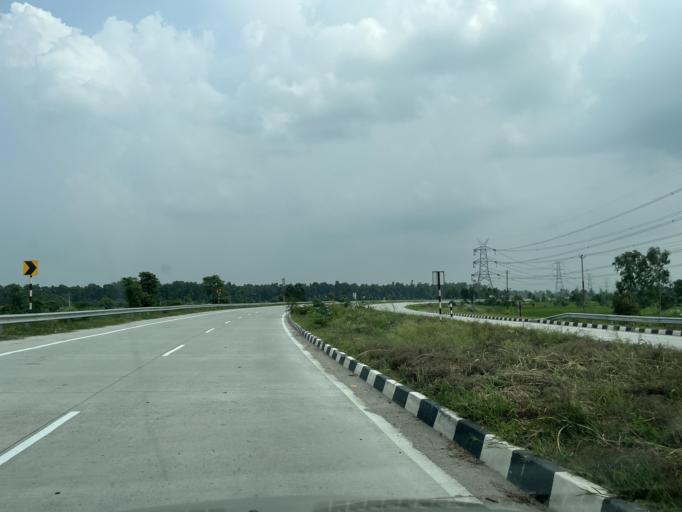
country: IN
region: Uttarakhand
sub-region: Udham Singh Nagar
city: Jaspur
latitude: 29.2806
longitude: 78.8656
